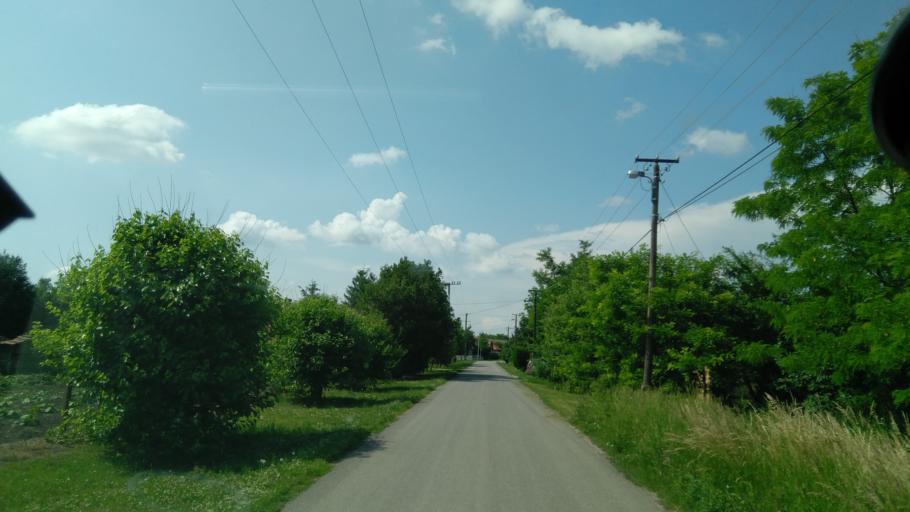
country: HU
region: Bekes
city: Doboz
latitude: 46.7355
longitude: 21.2304
